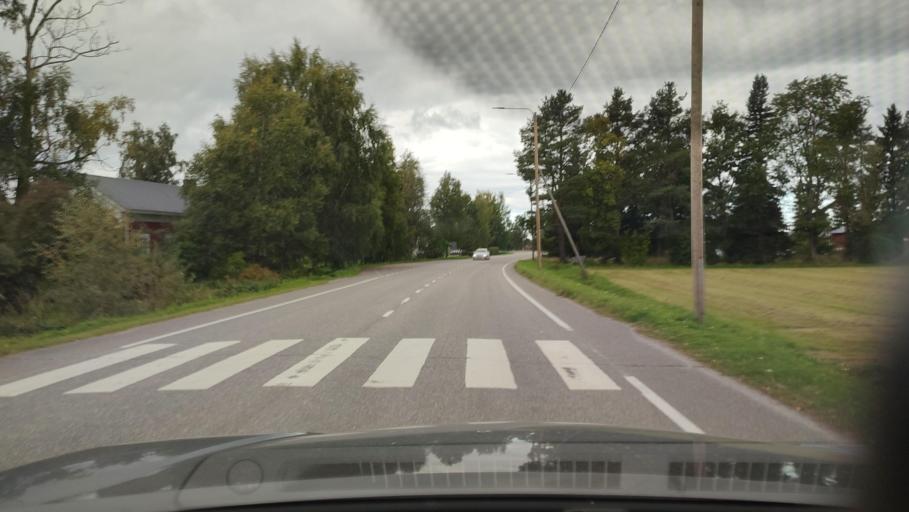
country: FI
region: Ostrobothnia
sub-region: Sydosterbotten
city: Kristinestad
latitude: 62.2574
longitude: 21.5257
